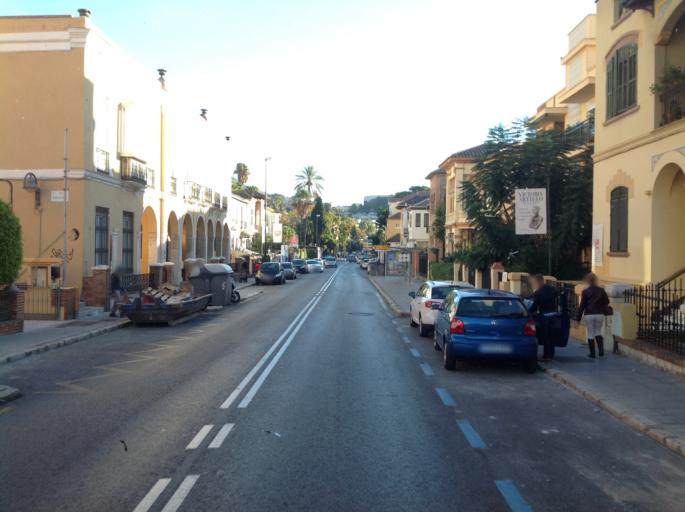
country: ES
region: Andalusia
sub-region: Provincia de Malaga
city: Malaga
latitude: 36.7218
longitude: -4.4014
